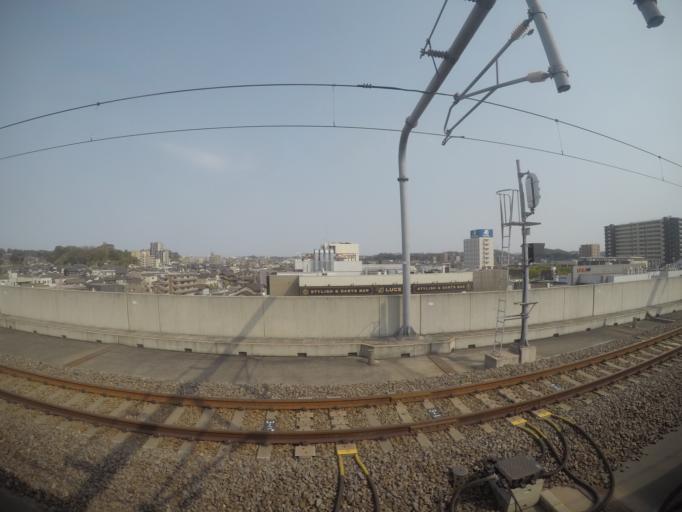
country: JP
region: Aichi
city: Obu
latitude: 35.0211
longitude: 136.8931
